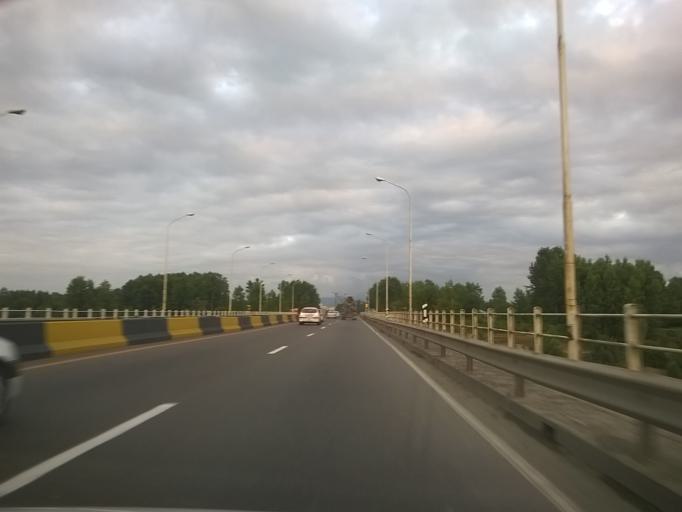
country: IR
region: Gilan
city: Astaneh-ye Ashrafiyeh
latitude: 37.2616
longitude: 49.9261
